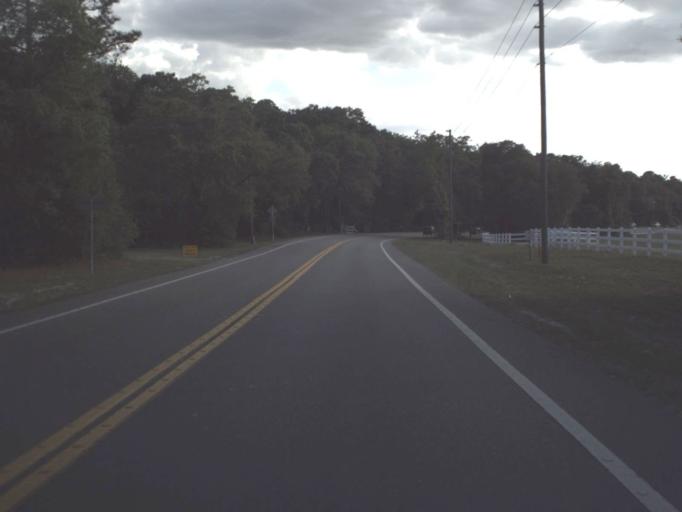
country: US
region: Florida
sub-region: Lake County
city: Mount Plymouth
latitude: 28.8071
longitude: -81.5692
